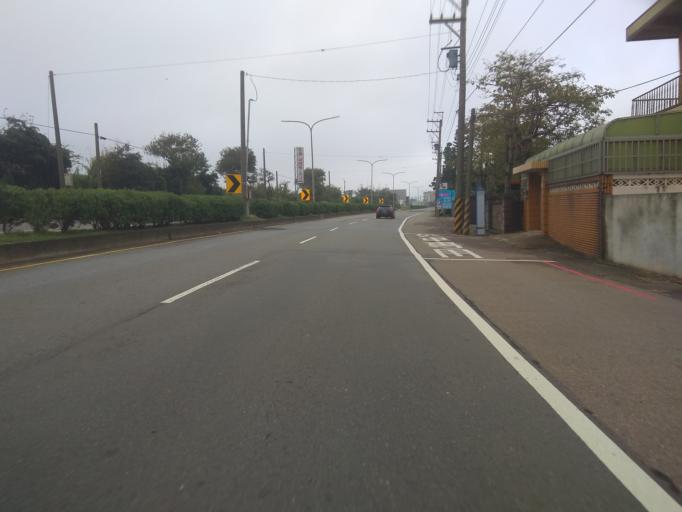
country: TW
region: Taiwan
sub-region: Hsinchu
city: Zhubei
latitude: 25.0036
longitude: 121.0398
